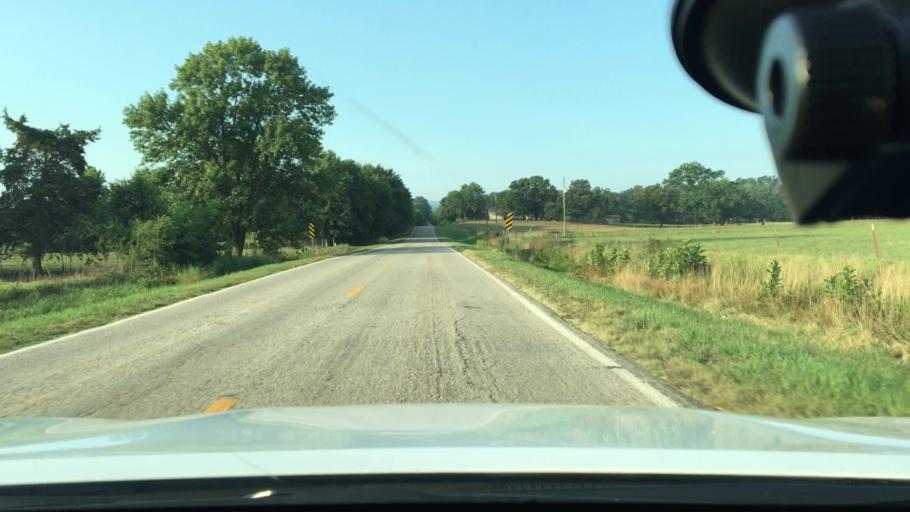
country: US
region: Arkansas
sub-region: Logan County
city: Paris
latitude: 35.3205
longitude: -93.6323
